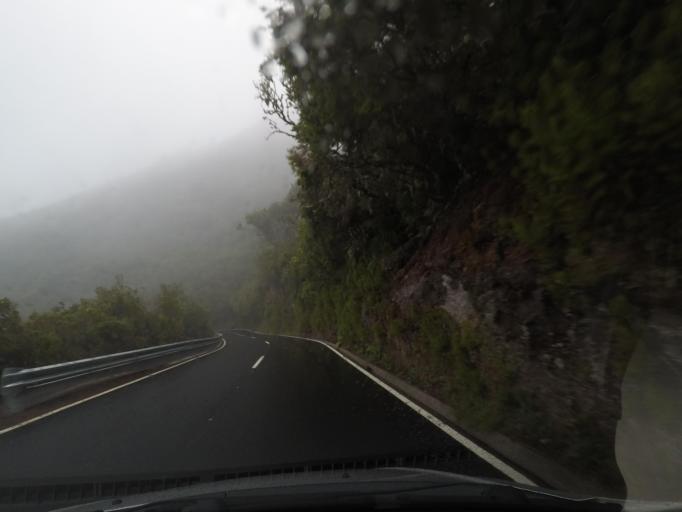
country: PT
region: Madeira
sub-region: Santana
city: Santana
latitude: 32.7688
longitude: -16.9169
